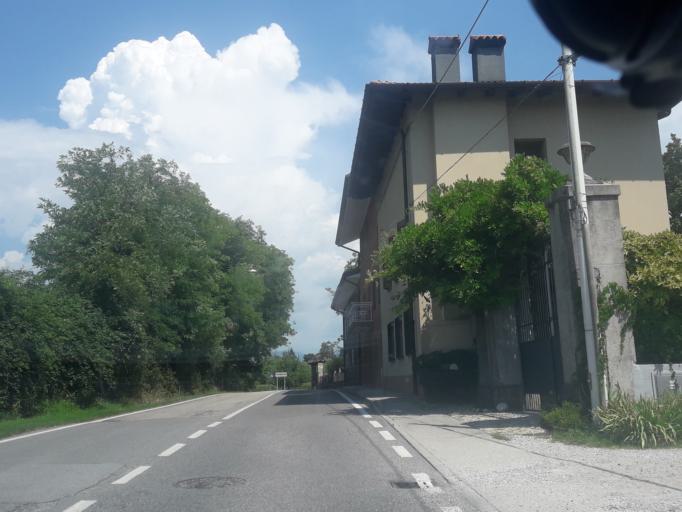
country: IT
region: Friuli Venezia Giulia
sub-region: Provincia di Udine
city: Pagnacco
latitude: 46.1193
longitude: 13.1828
